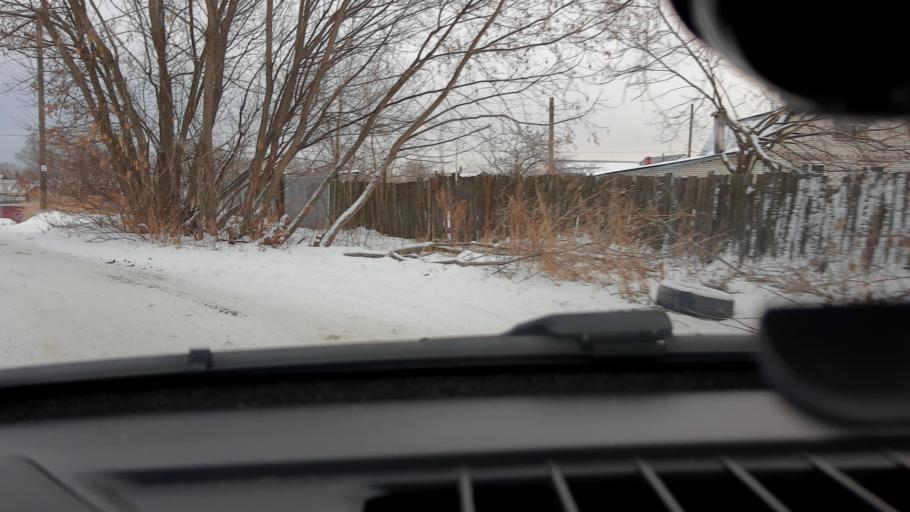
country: RU
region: Nizjnij Novgorod
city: Gorbatovka
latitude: 56.3730
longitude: 43.8241
